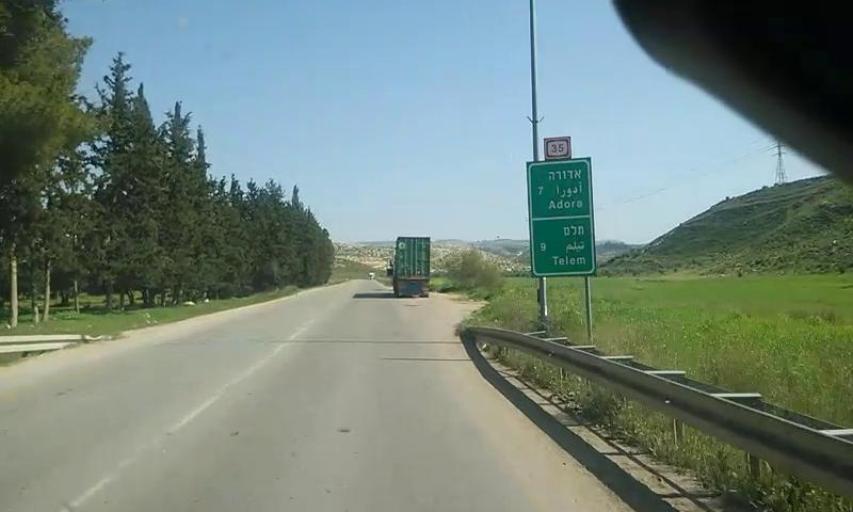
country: PS
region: West Bank
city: Idhna
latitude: 31.5902
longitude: 34.9663
